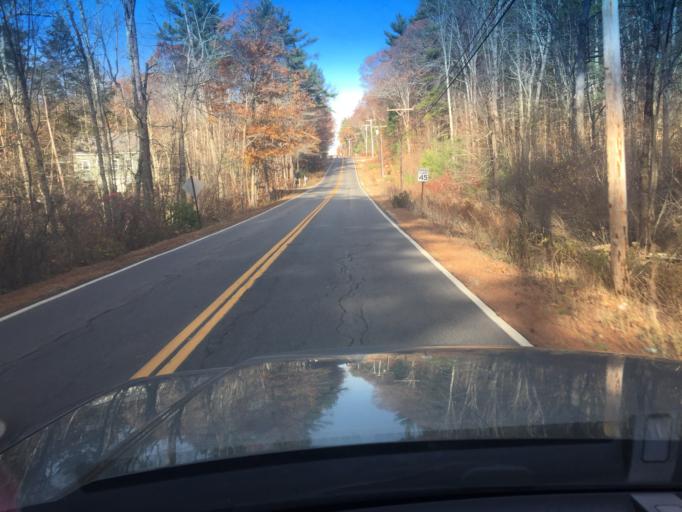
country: US
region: Maine
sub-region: York County
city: Eliot
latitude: 43.1865
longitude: -70.7448
